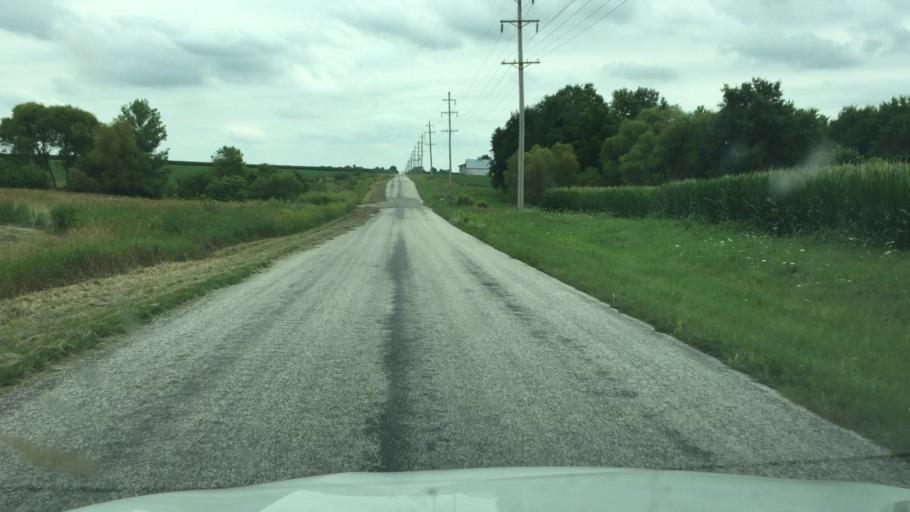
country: US
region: Illinois
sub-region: Hancock County
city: Carthage
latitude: 40.3462
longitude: -91.0822
